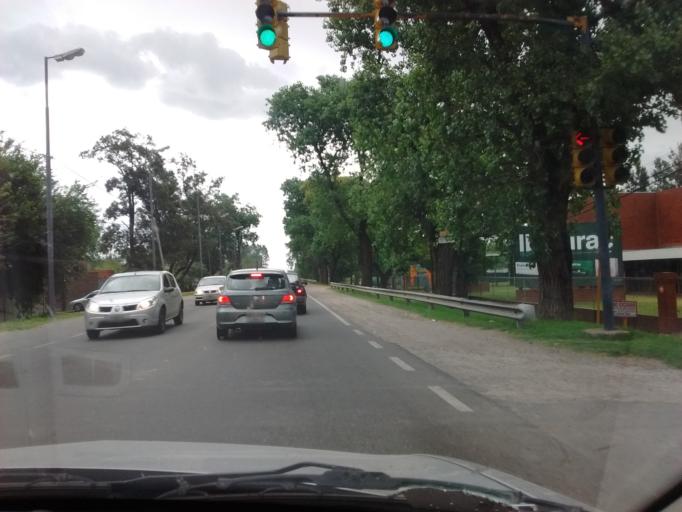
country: AR
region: Santa Fe
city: Funes
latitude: -32.9260
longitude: -60.7568
